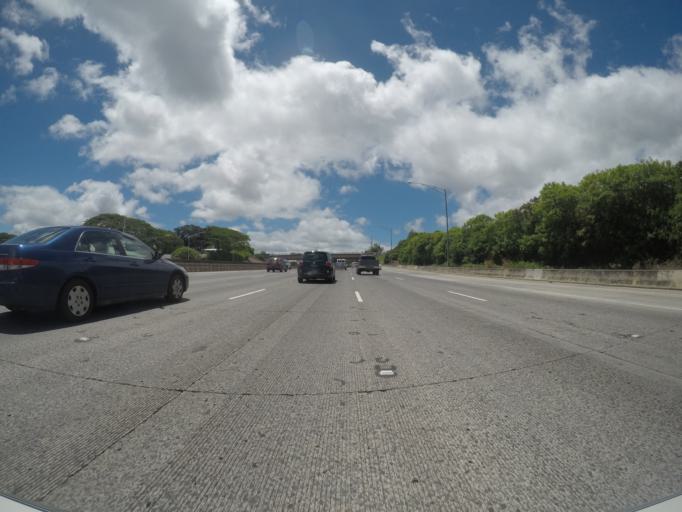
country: US
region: Hawaii
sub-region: Honolulu County
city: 'Aiea
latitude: 21.3830
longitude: -157.9313
